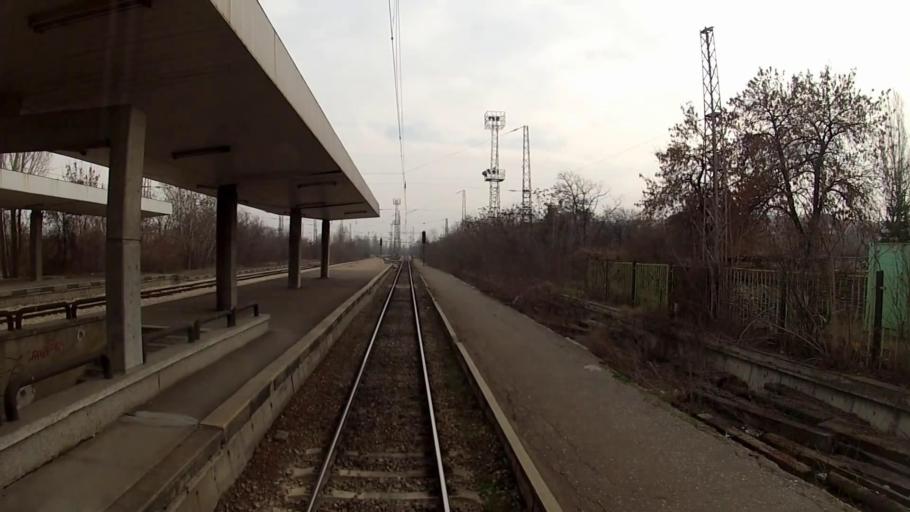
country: BG
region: Sofia-Capital
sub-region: Stolichna Obshtina
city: Sofia
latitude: 42.6869
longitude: 23.3791
